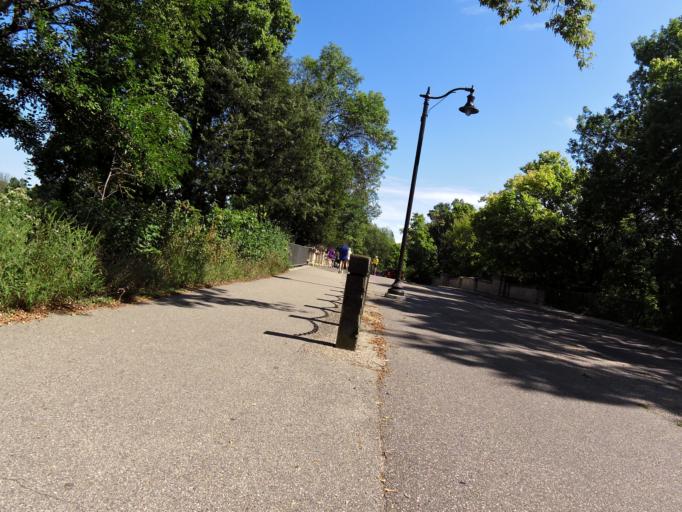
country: US
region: Minnesota
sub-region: Hennepin County
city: Saint Louis Park
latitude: 44.9513
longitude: -93.3067
